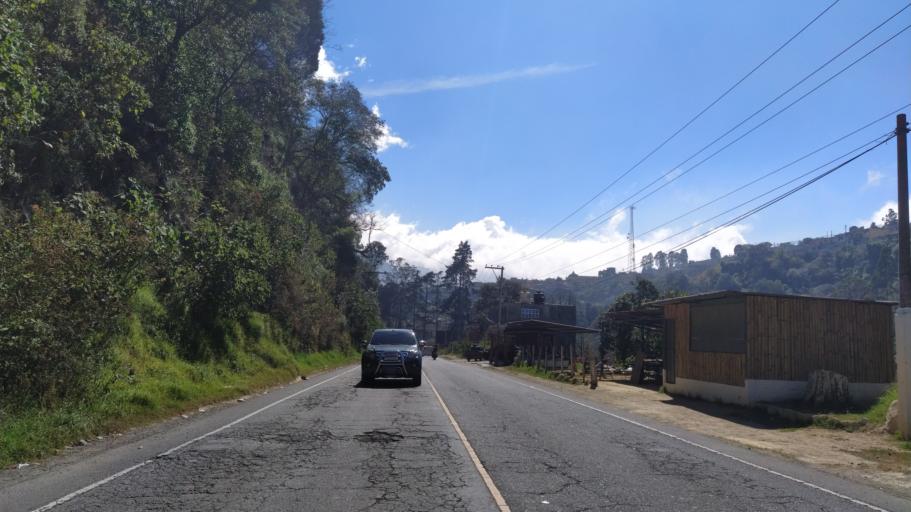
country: GT
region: Quetzaltenango
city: Cantel
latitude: 14.8172
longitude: -91.4529
